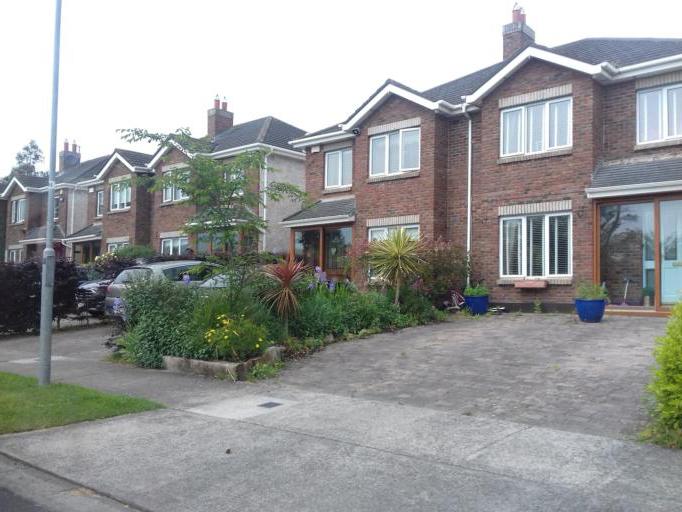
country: IE
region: Leinster
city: Kinsealy-Drinan
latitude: 53.4453
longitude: -6.1844
